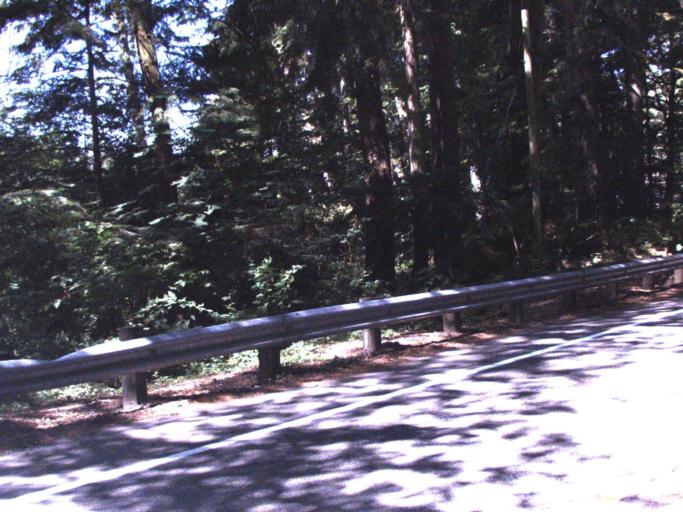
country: US
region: Washington
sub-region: King County
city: Enumclaw
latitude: 47.1636
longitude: -121.7405
